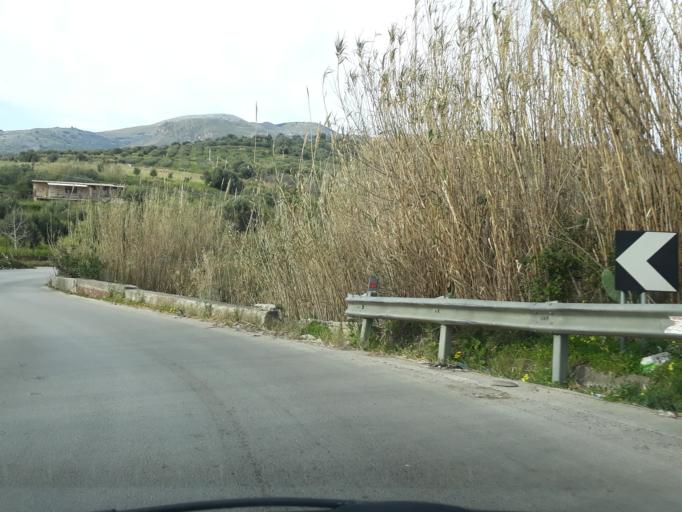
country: IT
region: Sicily
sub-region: Palermo
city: Giardinello
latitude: 38.0746
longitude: 13.1547
